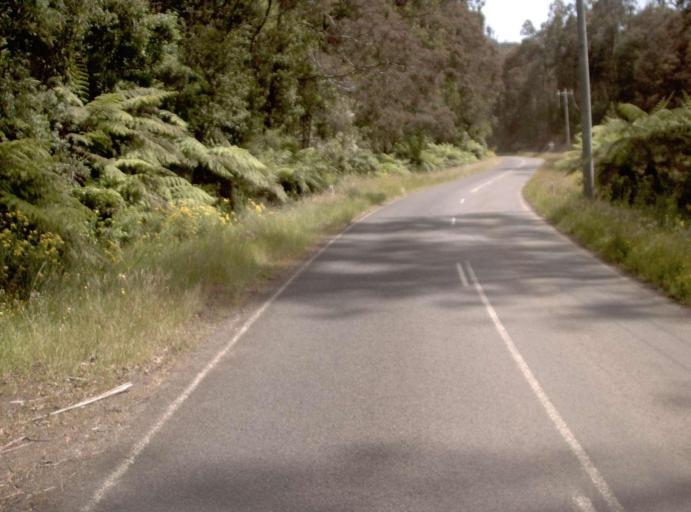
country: AU
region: Victoria
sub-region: Latrobe
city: Moe
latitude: -37.8728
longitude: 146.3770
